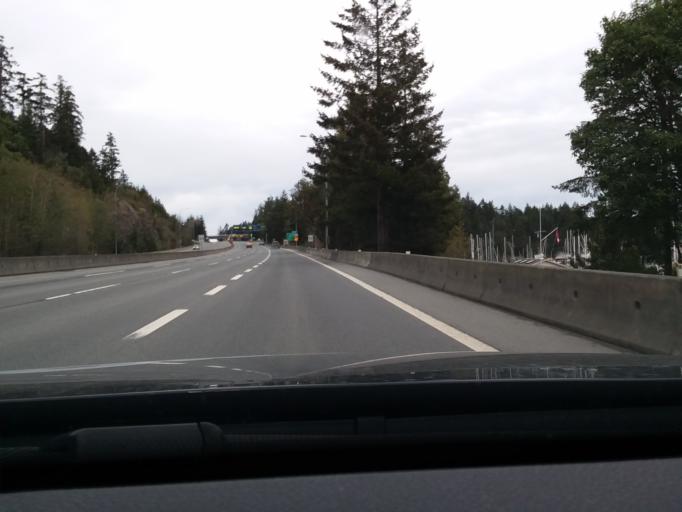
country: CA
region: British Columbia
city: North Saanich
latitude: 48.6803
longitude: -123.4177
